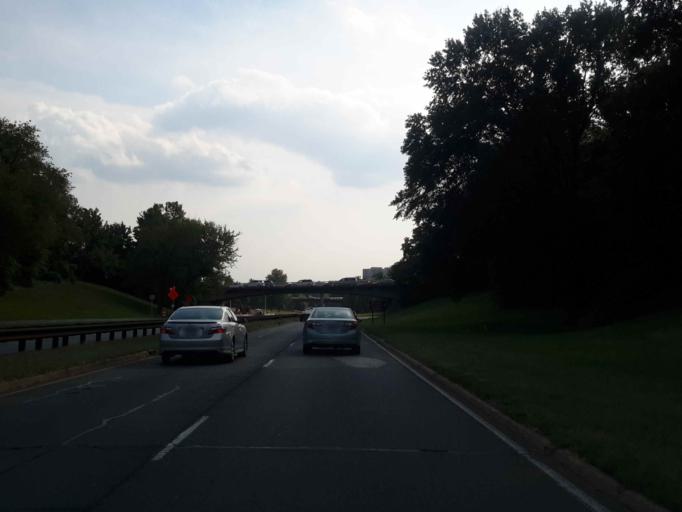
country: US
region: Washington, D.C.
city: Washington, D.C.
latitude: 38.8511
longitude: -77.0476
